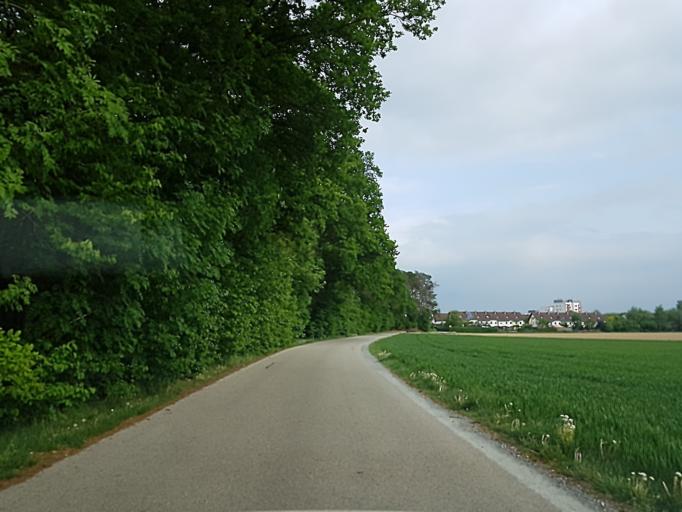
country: DE
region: Bavaria
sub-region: Upper Bavaria
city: Waldkraiburg
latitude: 48.2050
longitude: 12.3801
